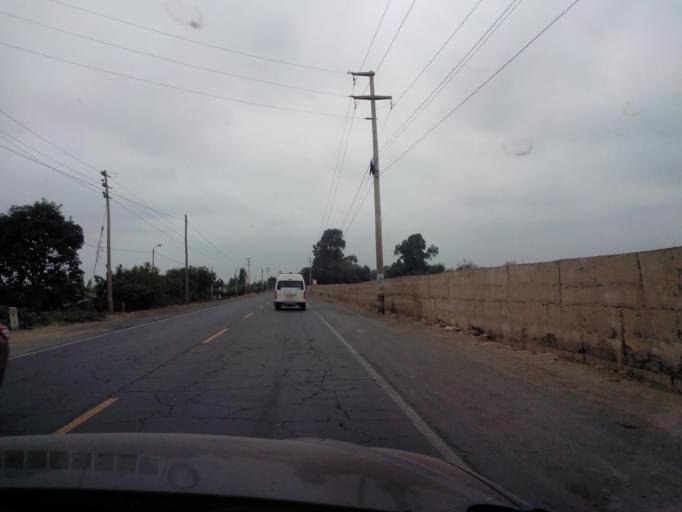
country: PE
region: Ica
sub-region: Provincia de Chincha
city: Chincha Baja
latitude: -13.5342
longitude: -76.1345
